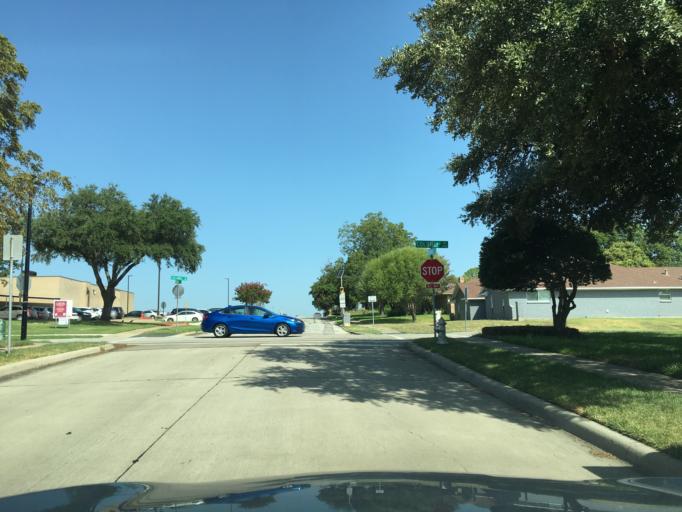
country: US
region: Texas
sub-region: Dallas County
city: Garland
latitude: 32.8785
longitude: -96.6098
